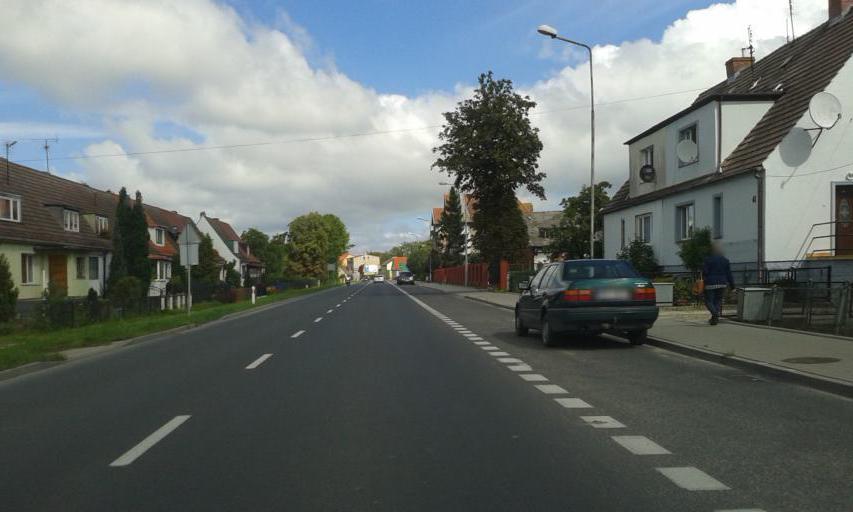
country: PL
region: West Pomeranian Voivodeship
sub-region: Powiat slawienski
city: Darlowo
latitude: 54.4132
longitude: 16.4105
